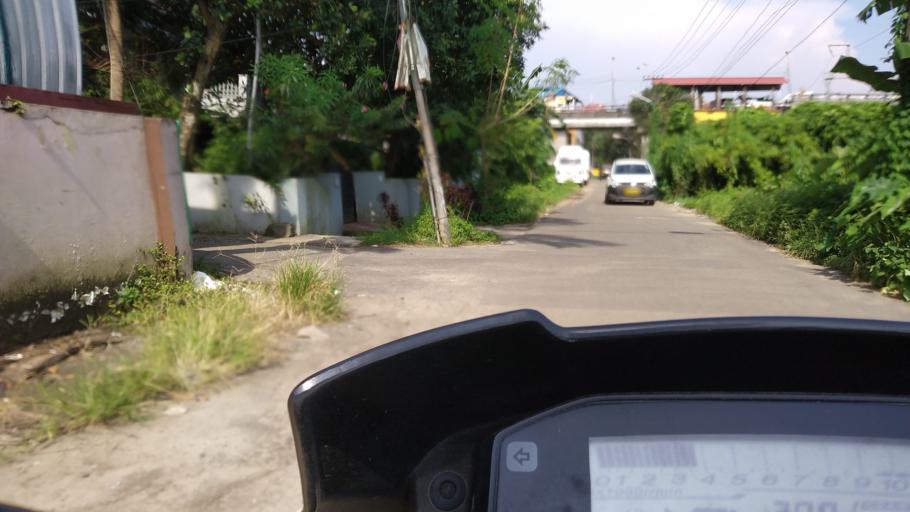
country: IN
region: Kerala
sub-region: Ernakulam
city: Cochin
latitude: 9.9809
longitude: 76.2954
